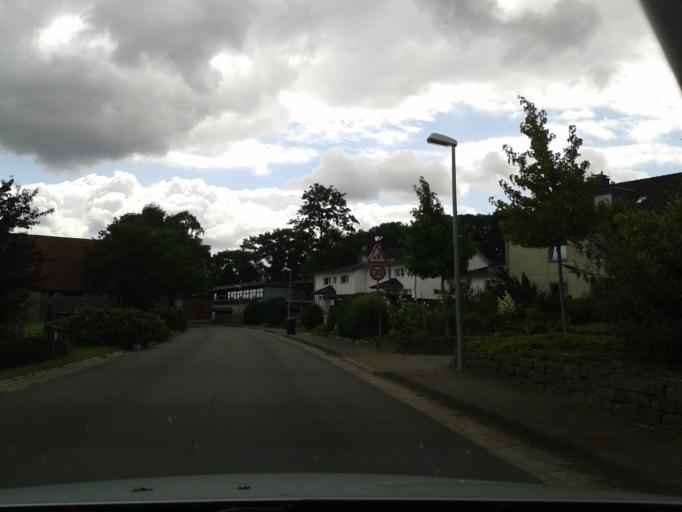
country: DE
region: North Rhine-Westphalia
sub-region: Regierungsbezirk Detmold
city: Barntrup
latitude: 52.0059
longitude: 9.0615
